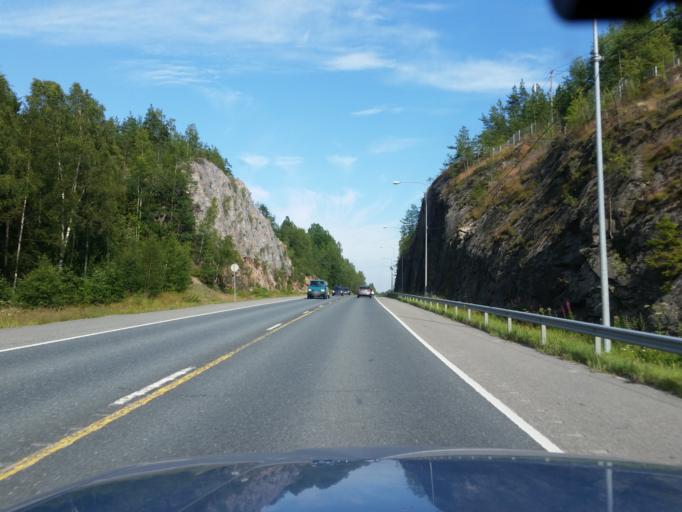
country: FI
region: Uusimaa
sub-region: Helsinki
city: Siuntio
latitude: 60.0963
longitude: 24.2606
